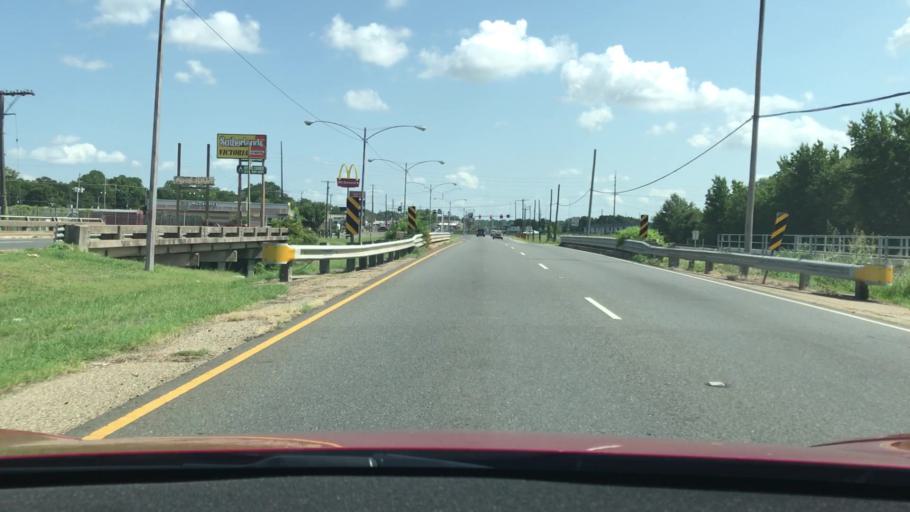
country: US
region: Louisiana
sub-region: Bossier Parish
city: Bossier City
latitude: 32.4397
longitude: -93.7816
